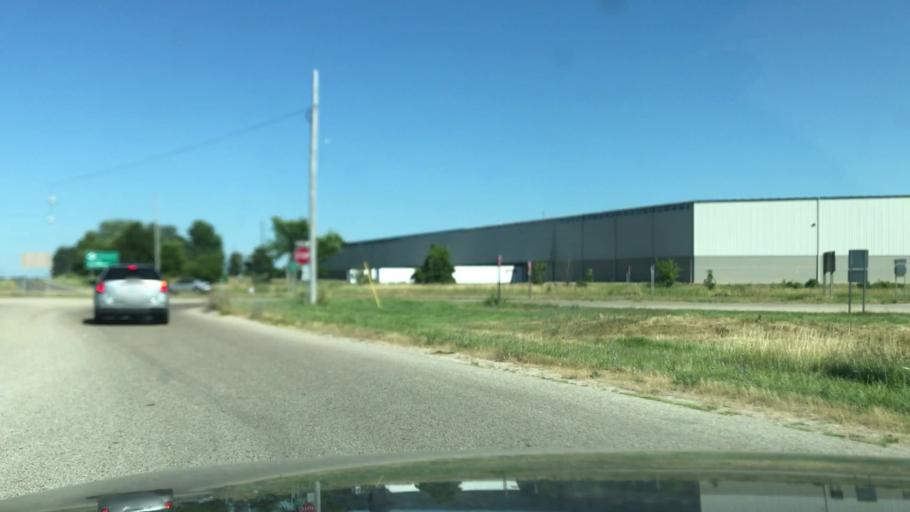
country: US
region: Michigan
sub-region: Ottawa County
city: Zeeland
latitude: 42.8195
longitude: -85.9882
